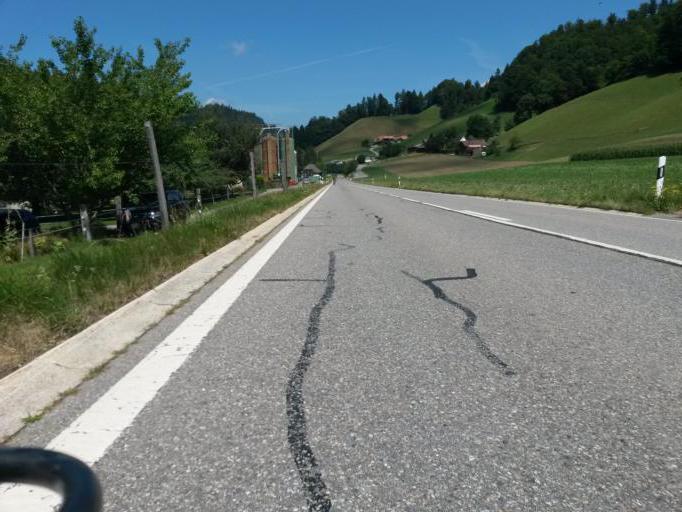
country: CH
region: Bern
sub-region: Bern-Mittelland District
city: Walkringen
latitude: 46.9577
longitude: 7.6212
